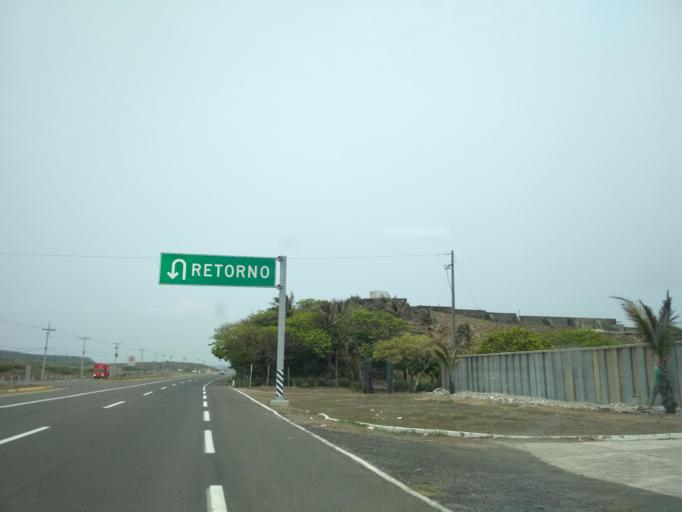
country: MX
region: Veracruz
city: Anton Lizardo
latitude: 19.0531
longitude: -96.0275
